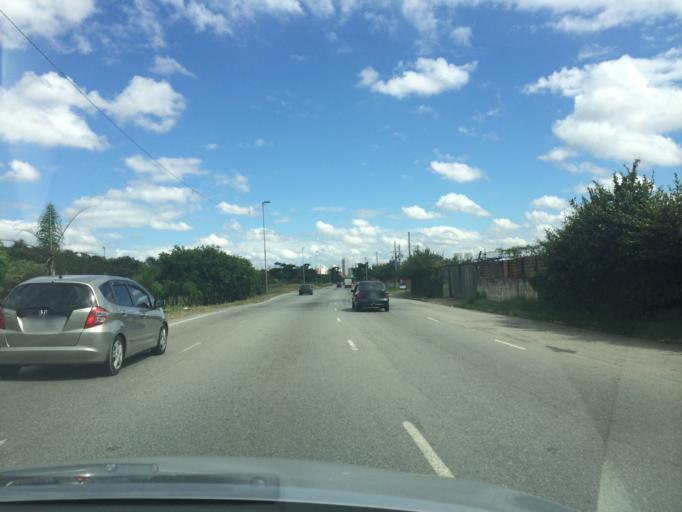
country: BR
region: Sao Paulo
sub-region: Guarulhos
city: Guarulhos
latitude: -23.5084
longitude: -46.5590
